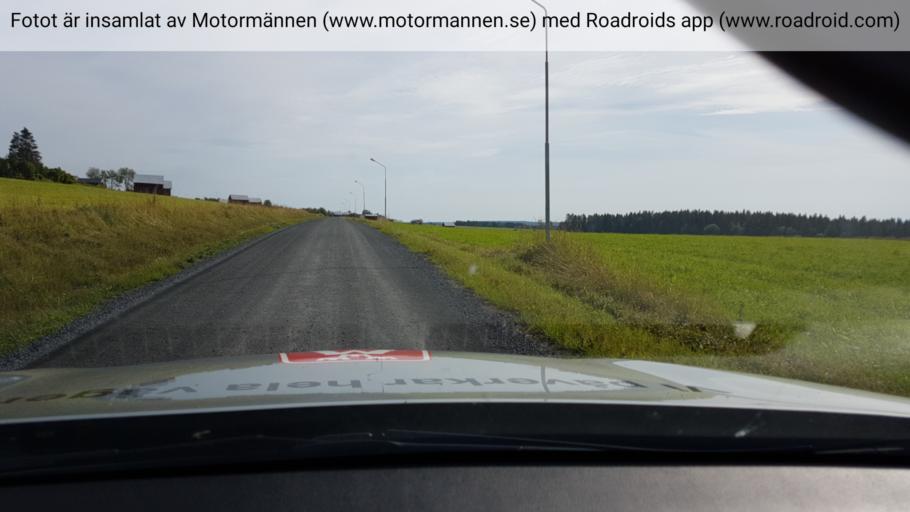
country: SE
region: Jaemtland
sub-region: Krokoms Kommun
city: Valla
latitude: 63.3633
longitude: 13.9616
